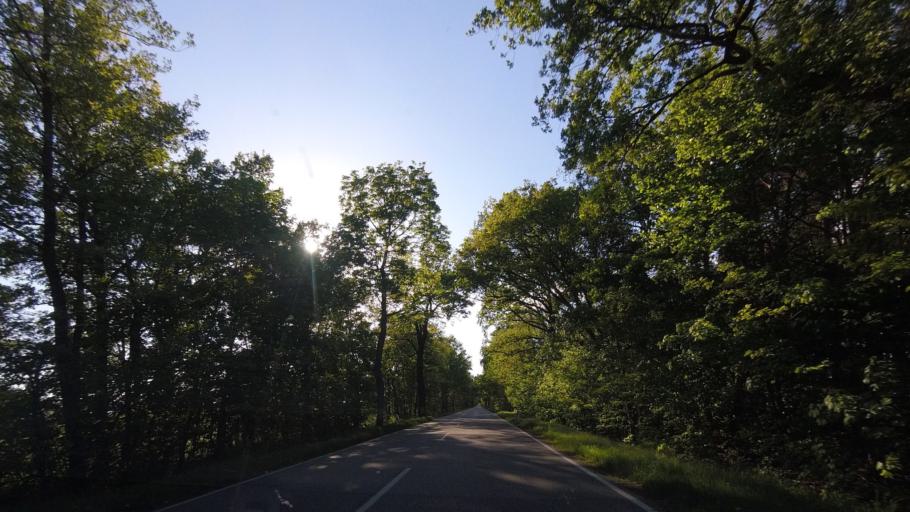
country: DE
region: Brandenburg
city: Kasel-Golzig
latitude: 51.9556
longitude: 13.7568
